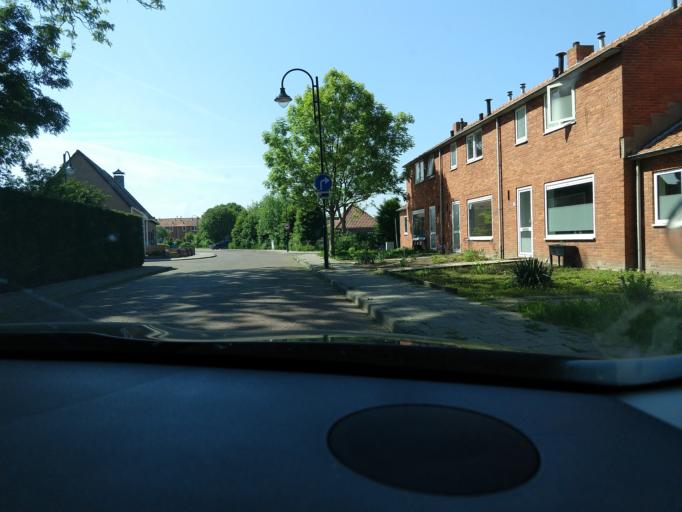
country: NL
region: Zeeland
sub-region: Gemeente Reimerswaal
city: Yerseke
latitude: 51.5493
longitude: 4.0761
